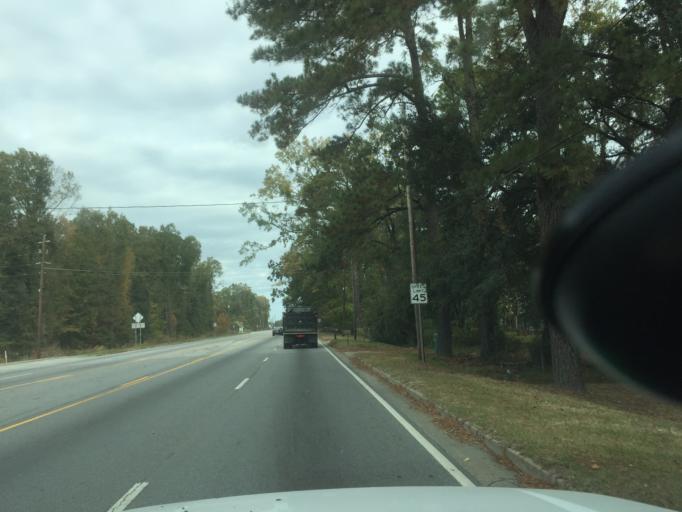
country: US
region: Georgia
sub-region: Chatham County
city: Garden City
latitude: 32.0978
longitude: -81.1962
